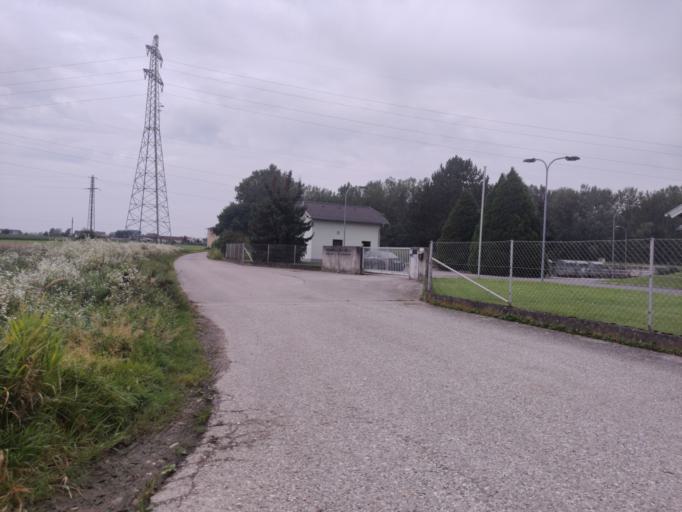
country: AT
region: Lower Austria
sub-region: Politischer Bezirk Amstetten
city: Ennsdorf
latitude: 48.2301
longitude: 14.5358
